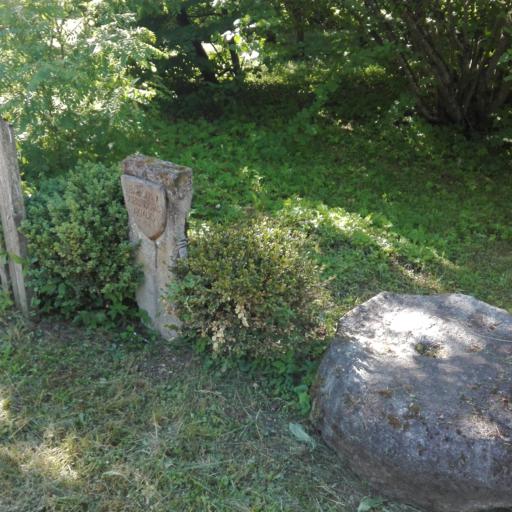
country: LT
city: Vabalninkas
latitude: 56.0364
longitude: 24.7076
